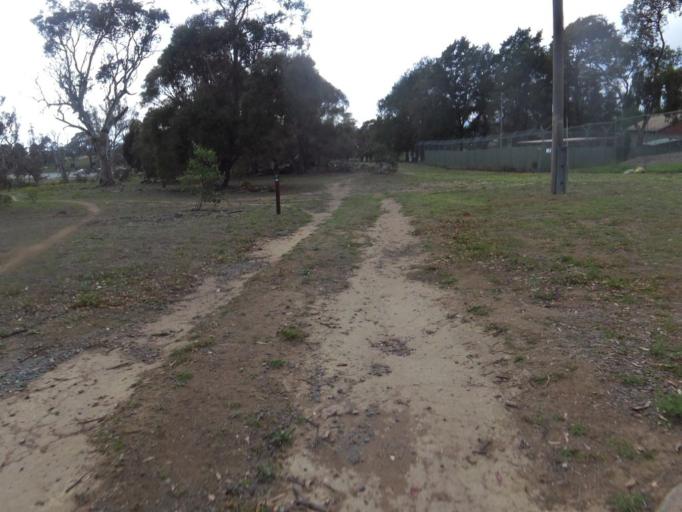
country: AU
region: Australian Capital Territory
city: Forrest
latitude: -35.3457
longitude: 149.1371
